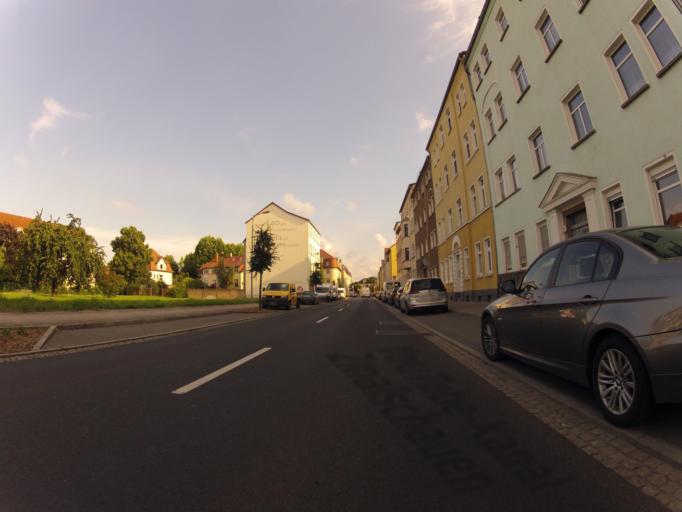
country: DE
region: Saxony
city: Wurzen
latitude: 51.3681
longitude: 12.7450
